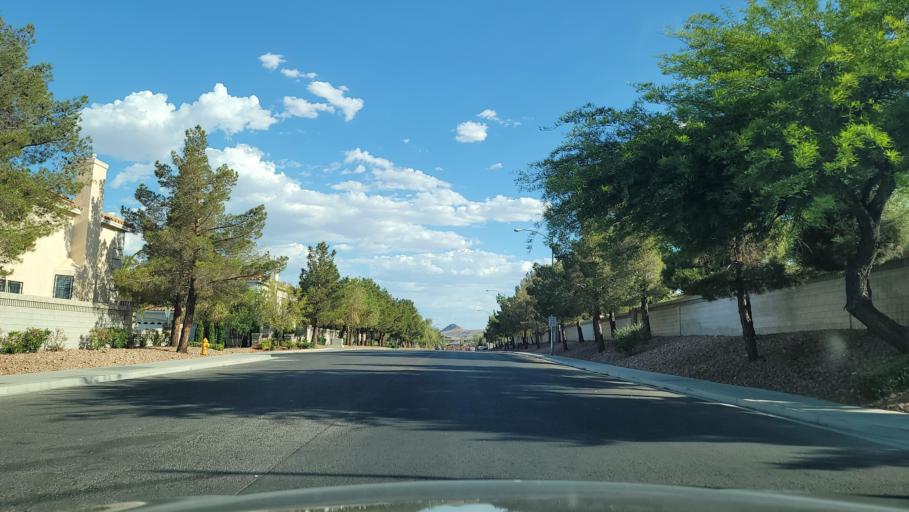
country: US
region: Nevada
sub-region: Clark County
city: Summerlin South
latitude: 36.0964
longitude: -115.3019
